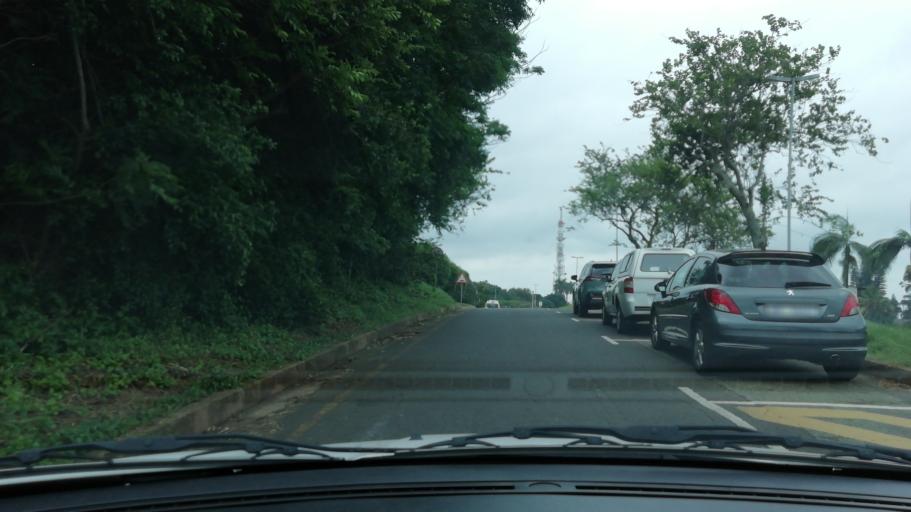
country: ZA
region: KwaZulu-Natal
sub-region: uThungulu District Municipality
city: Empangeni
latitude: -28.7476
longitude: 31.8898
